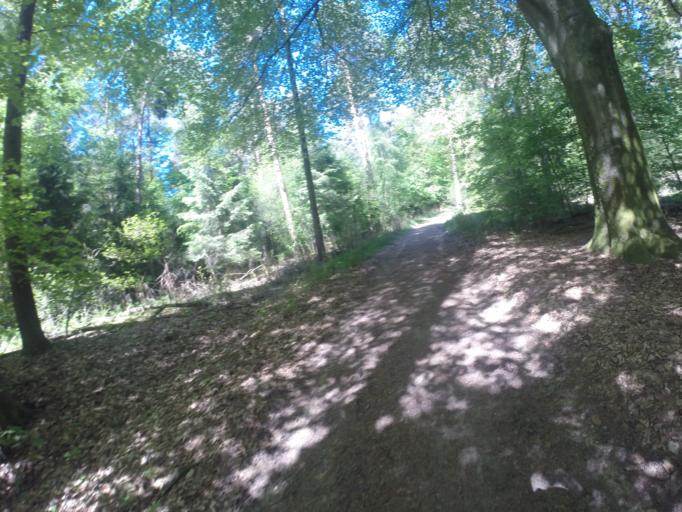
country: NL
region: Gelderland
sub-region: Gemeente Montferland
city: s-Heerenberg
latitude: 51.9091
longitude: 6.2370
